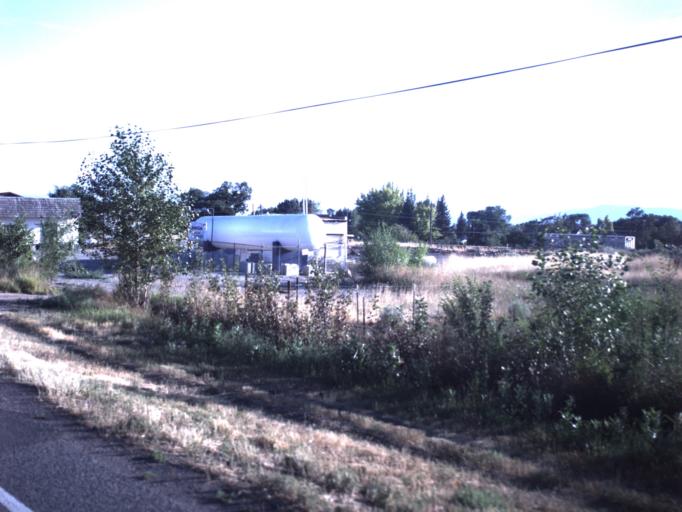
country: US
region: Utah
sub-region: Sanpete County
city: Mount Pleasant
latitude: 39.5560
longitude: -111.4555
